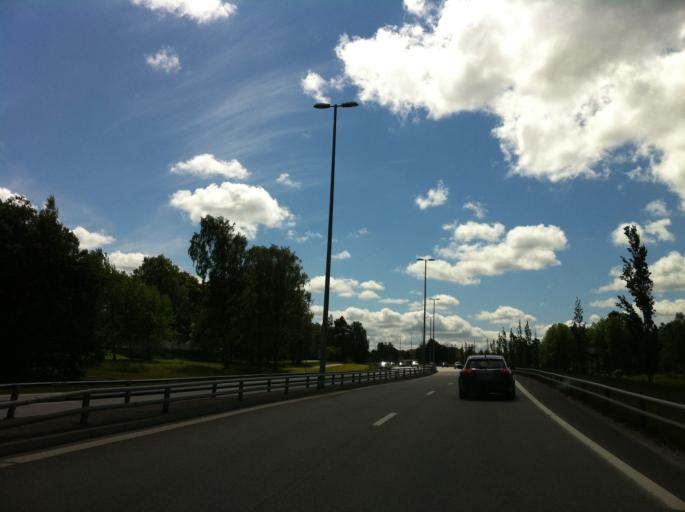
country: SE
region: Vaestra Goetaland
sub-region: Trollhattan
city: Trollhattan
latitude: 58.2844
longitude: 12.3071
